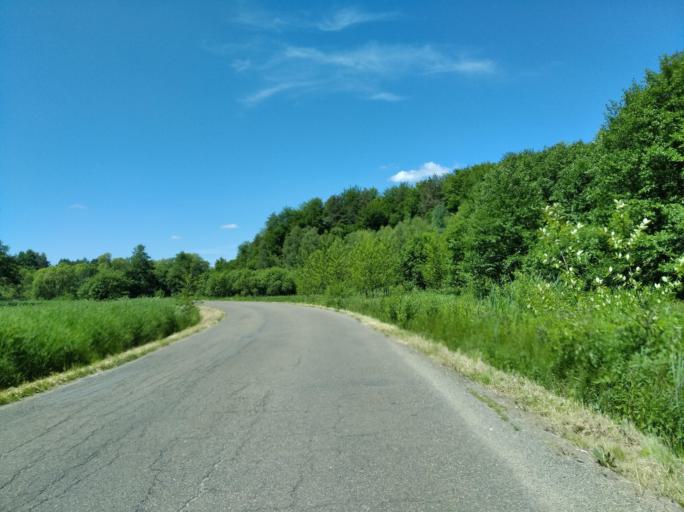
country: PL
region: Subcarpathian Voivodeship
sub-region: Powiat krosnienski
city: Chorkowka
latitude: 49.6370
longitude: 21.6019
